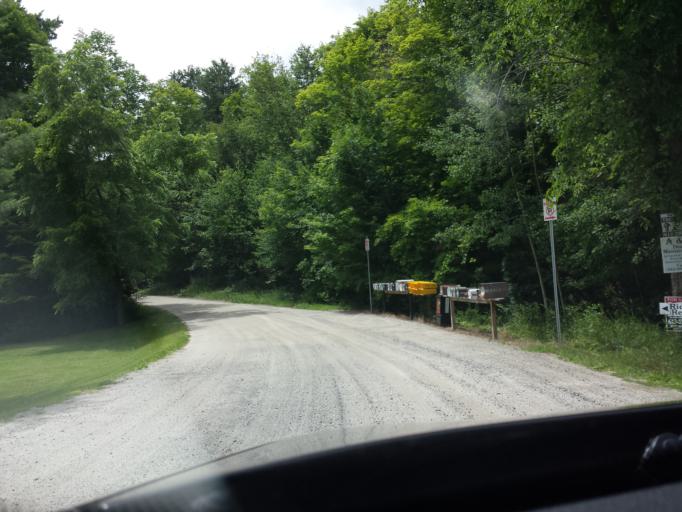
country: CA
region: Ontario
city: Perth
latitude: 44.8227
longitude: -76.2256
